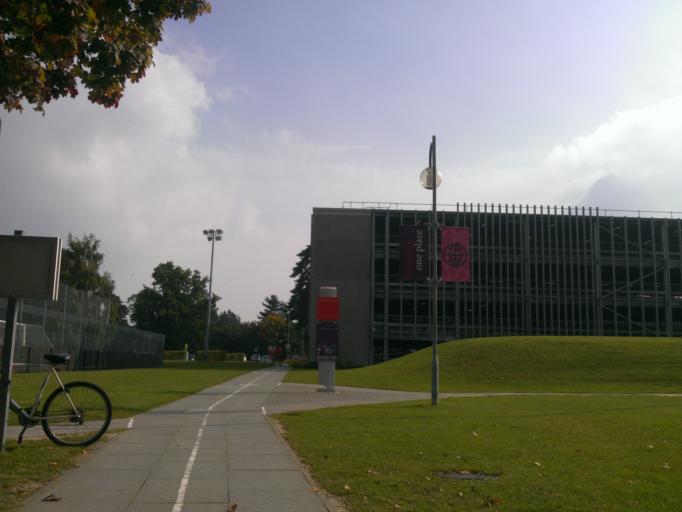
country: GB
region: England
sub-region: Essex
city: Rowhedge
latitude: 51.8753
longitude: 0.9492
